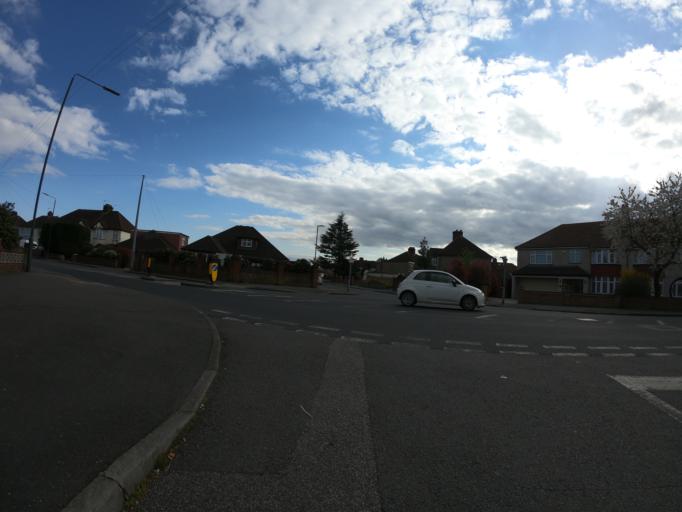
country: GB
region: England
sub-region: Greater London
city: Bexleyheath
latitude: 51.4721
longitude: 0.1513
